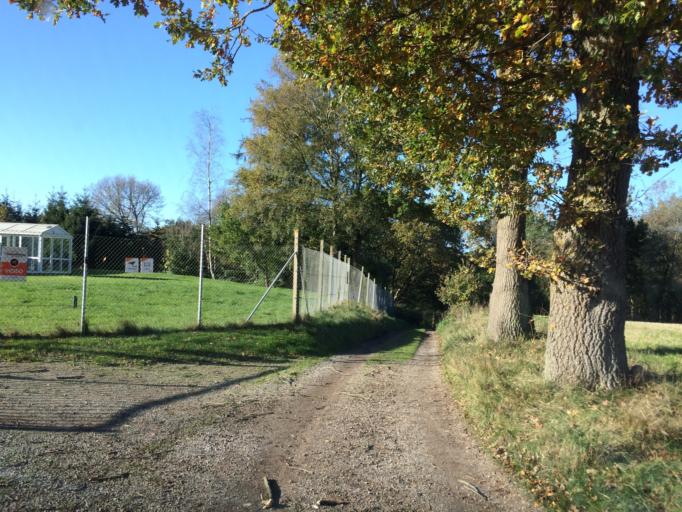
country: DK
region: South Denmark
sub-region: Fredericia Kommune
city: Taulov
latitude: 55.5687
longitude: 9.6345
